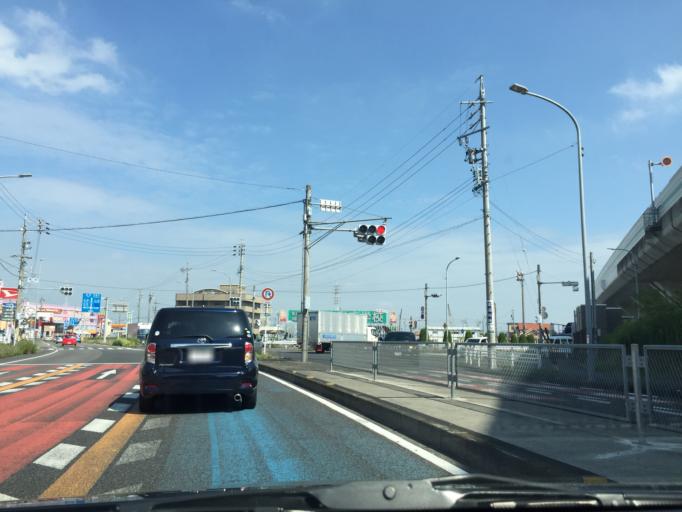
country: JP
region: Aichi
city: Ichinomiya
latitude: 35.3074
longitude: 136.7736
